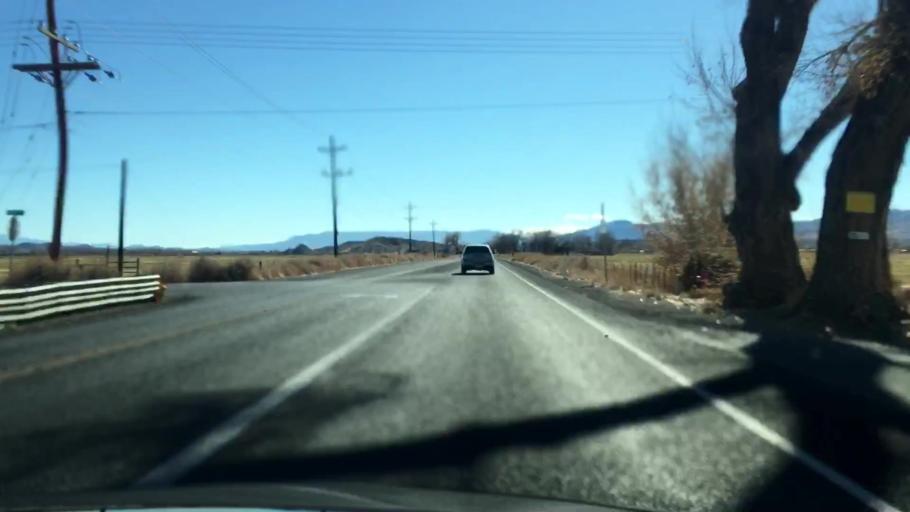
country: US
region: Nevada
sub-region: Lyon County
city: Yerington
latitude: 39.0483
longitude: -119.1815
